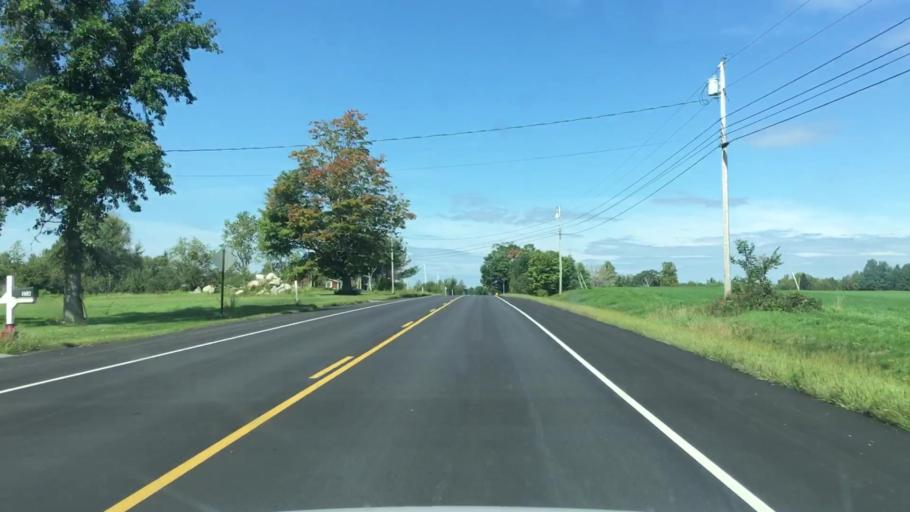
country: US
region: Maine
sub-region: Penobscot County
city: Corinna
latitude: 44.9532
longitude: -69.2564
